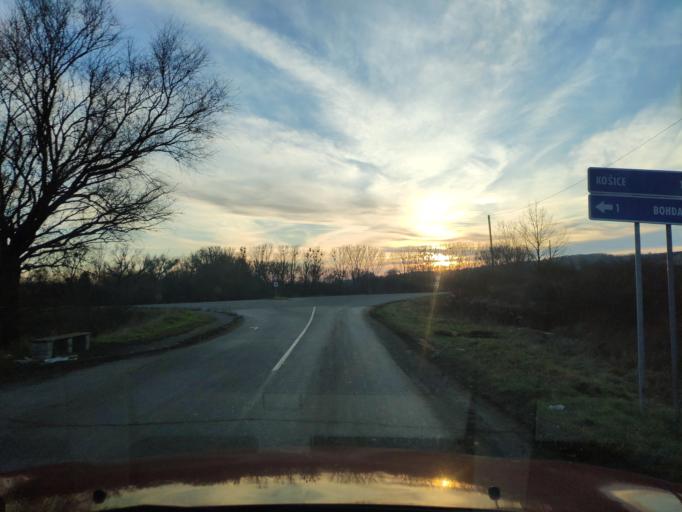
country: SK
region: Kosicky
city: Kosice
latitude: 48.6605
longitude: 21.3919
